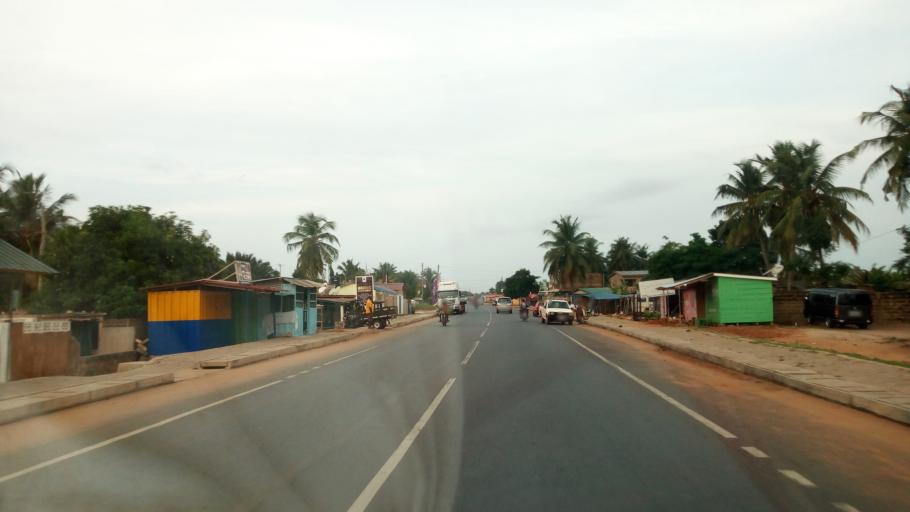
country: TG
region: Maritime
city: Lome
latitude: 6.1079
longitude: 1.1552
